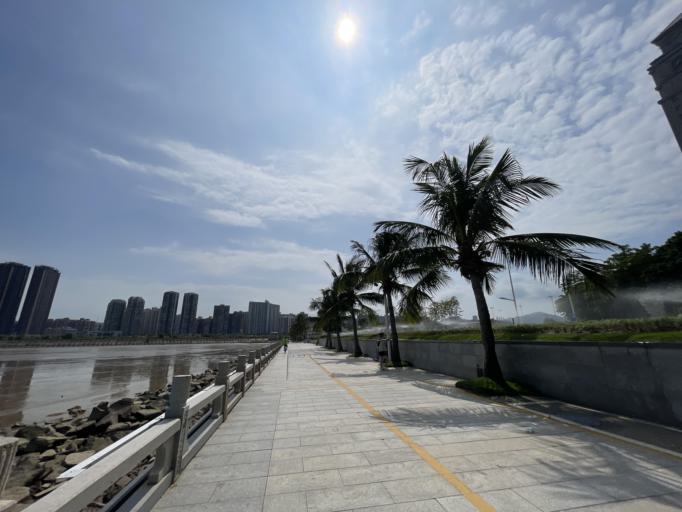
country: MO
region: Macau
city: Macau
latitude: 22.2207
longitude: 113.5538
